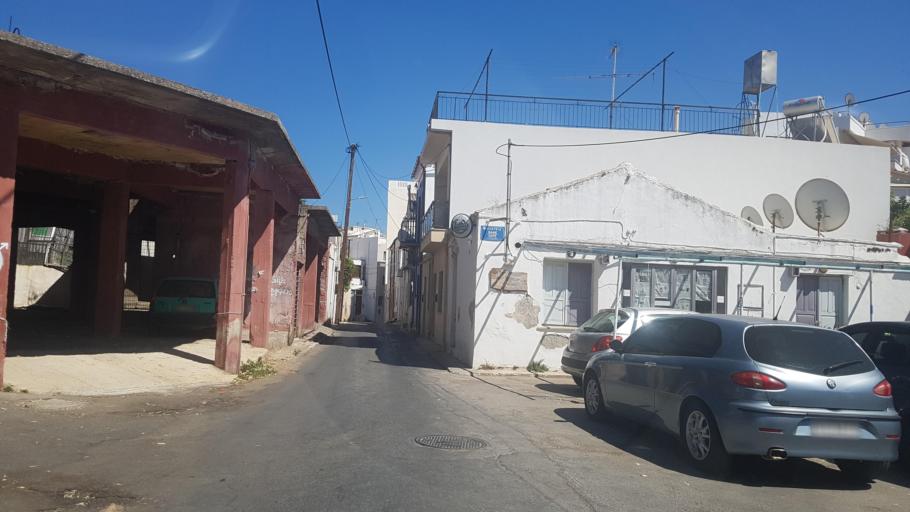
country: GR
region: Crete
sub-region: Nomos Chanias
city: Chania
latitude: 35.5138
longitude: 24.0109
